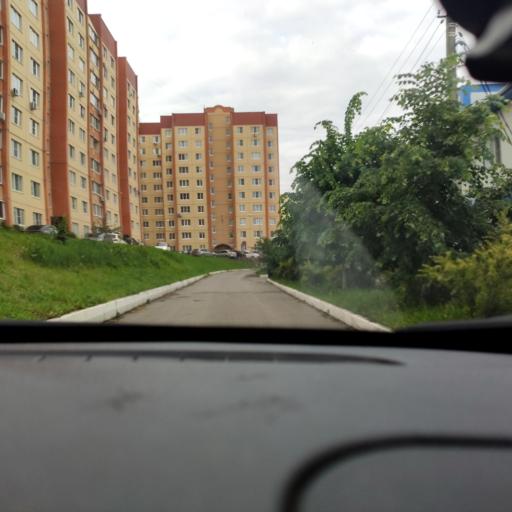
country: RU
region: Voronezj
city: Pridonskoy
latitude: 51.6229
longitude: 39.0639
